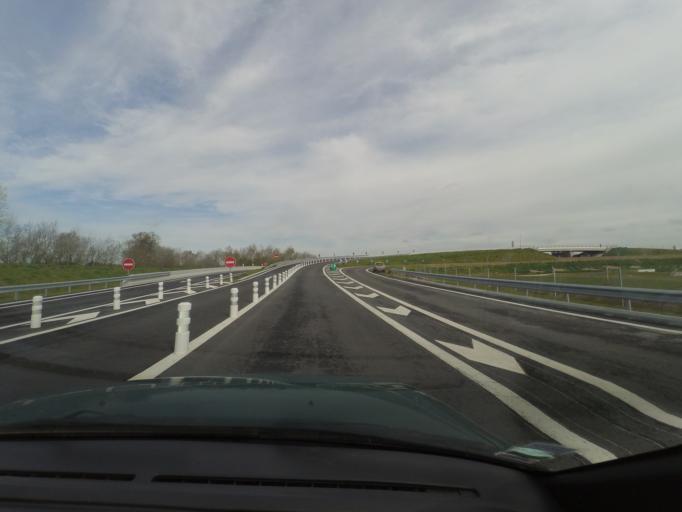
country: FR
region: Pays de la Loire
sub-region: Departement de la Loire-Atlantique
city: Aigrefeuille-sur-Maine
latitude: 47.0710
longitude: -1.4385
